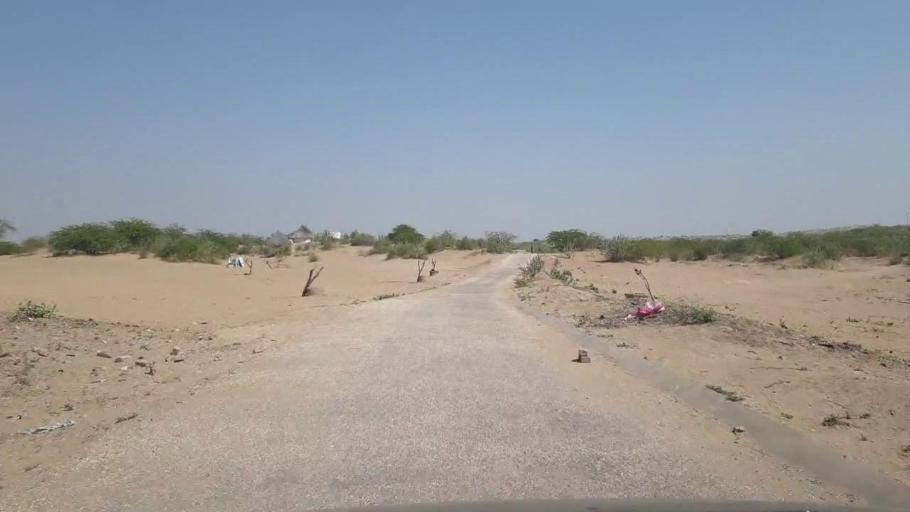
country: PK
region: Sindh
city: Chor
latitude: 25.5719
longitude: 70.1898
